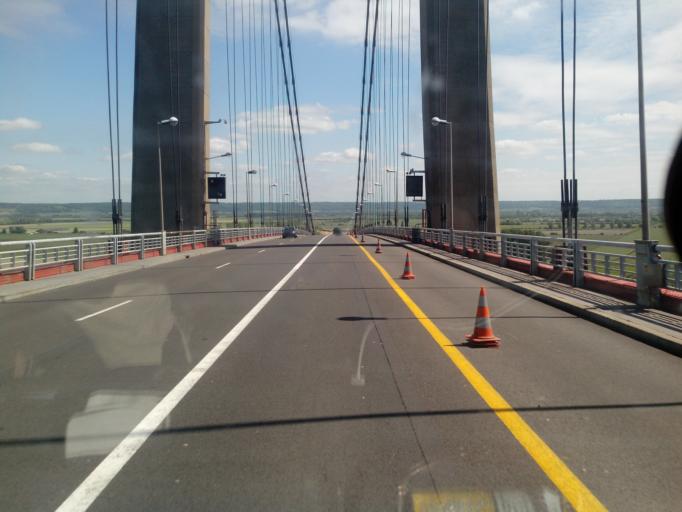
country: FR
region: Haute-Normandie
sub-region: Departement de la Seine-Maritime
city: Tancarville
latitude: 49.4710
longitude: 0.4666
